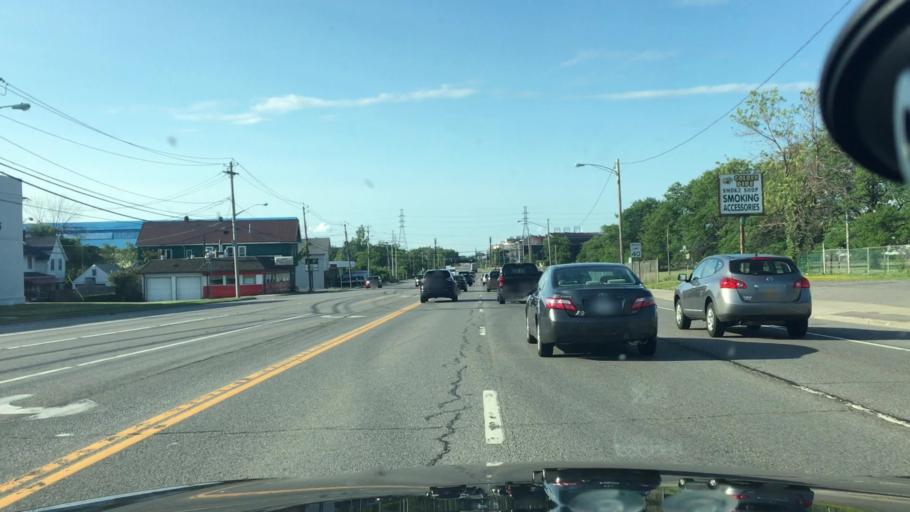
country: US
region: New York
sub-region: Erie County
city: Blasdell
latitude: 42.7982
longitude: -78.8467
